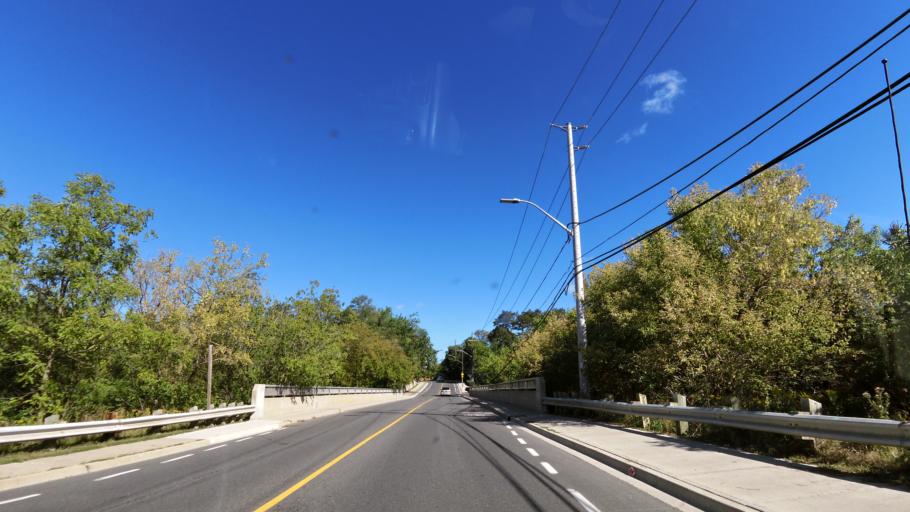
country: CA
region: Ontario
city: Mississauga
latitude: 43.5829
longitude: -79.7090
